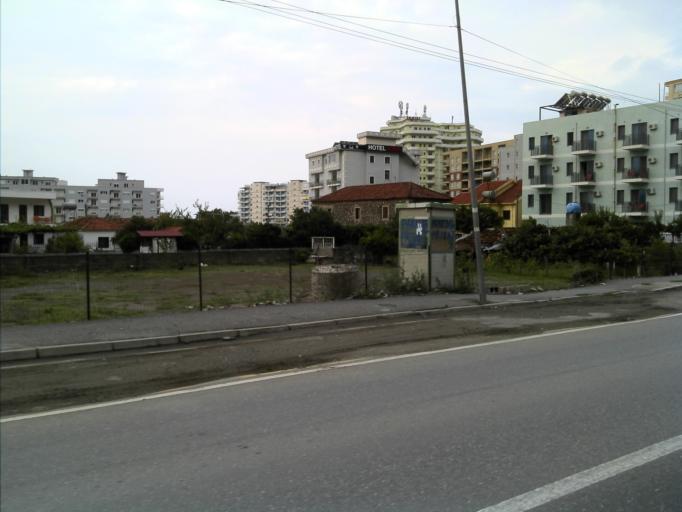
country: AL
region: Lezhe
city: Shengjin
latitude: 41.8089
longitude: 19.6022
